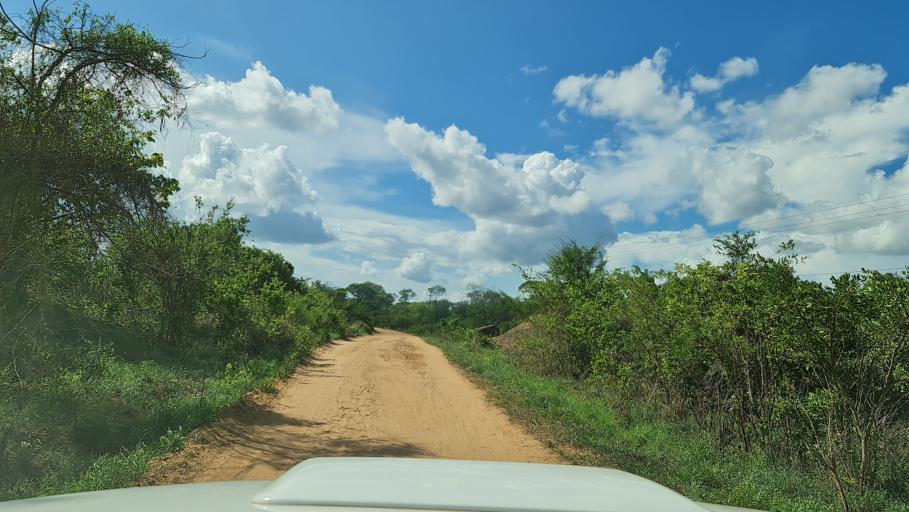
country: MZ
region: Nampula
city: Ilha de Mocambique
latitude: -15.4381
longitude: 40.2829
